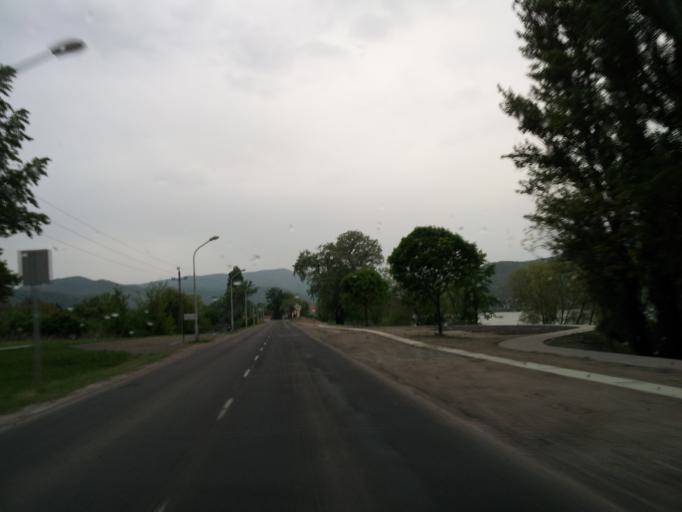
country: HU
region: Pest
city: Visegrad
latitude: 47.7901
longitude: 18.9706
